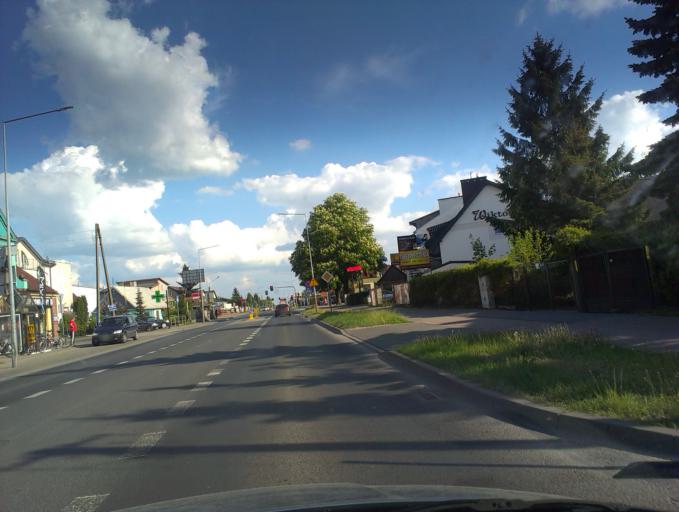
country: PL
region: Masovian Voivodeship
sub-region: Radom
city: Radom
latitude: 51.3803
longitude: 21.1820
